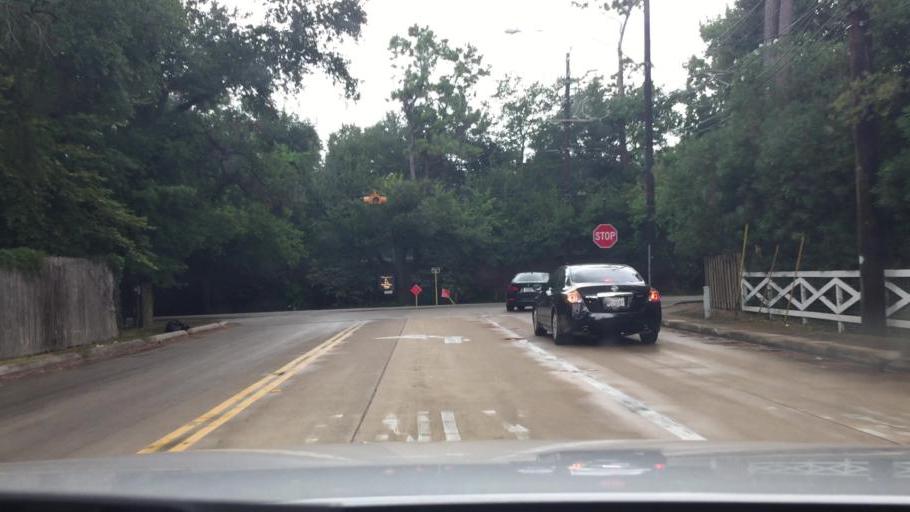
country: US
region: Texas
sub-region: Harris County
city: Hedwig Village
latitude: 29.7737
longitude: -95.5213
